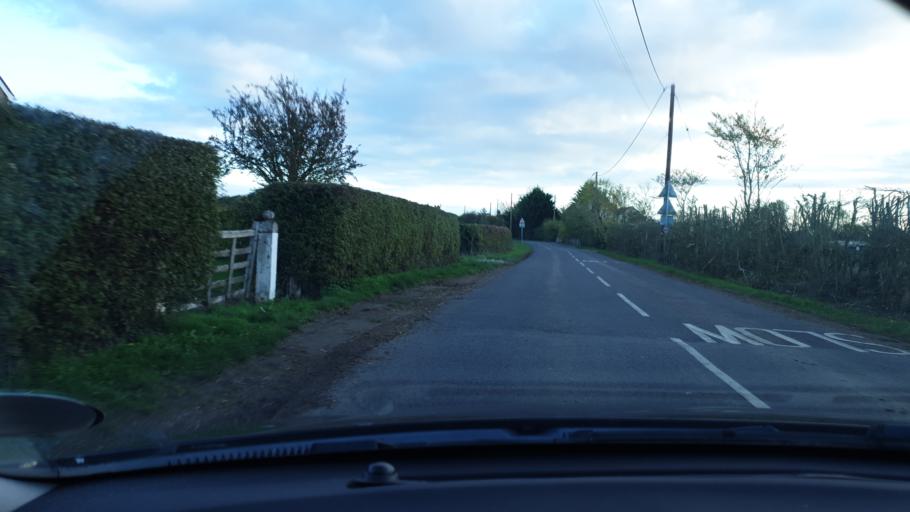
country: GB
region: England
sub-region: Essex
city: Little Clacton
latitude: 51.8981
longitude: 1.1453
